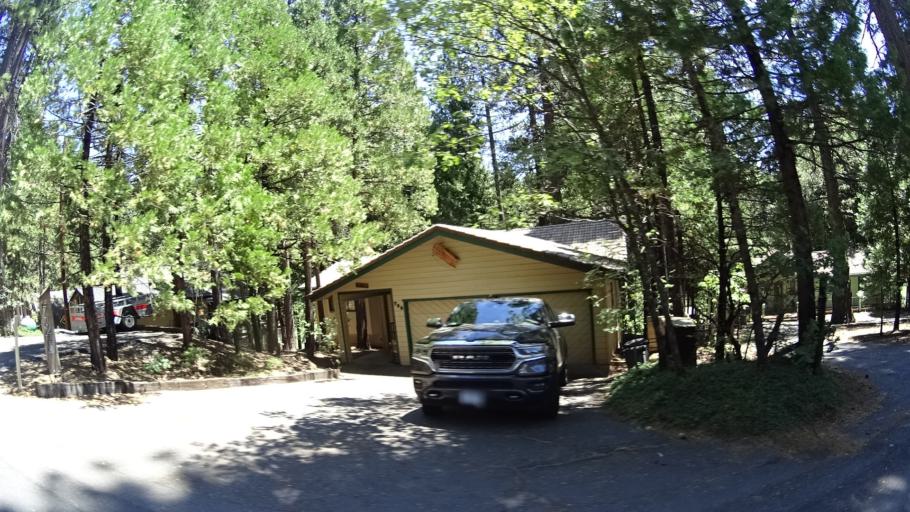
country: US
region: California
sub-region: Calaveras County
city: Arnold
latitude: 38.2537
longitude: -120.3308
